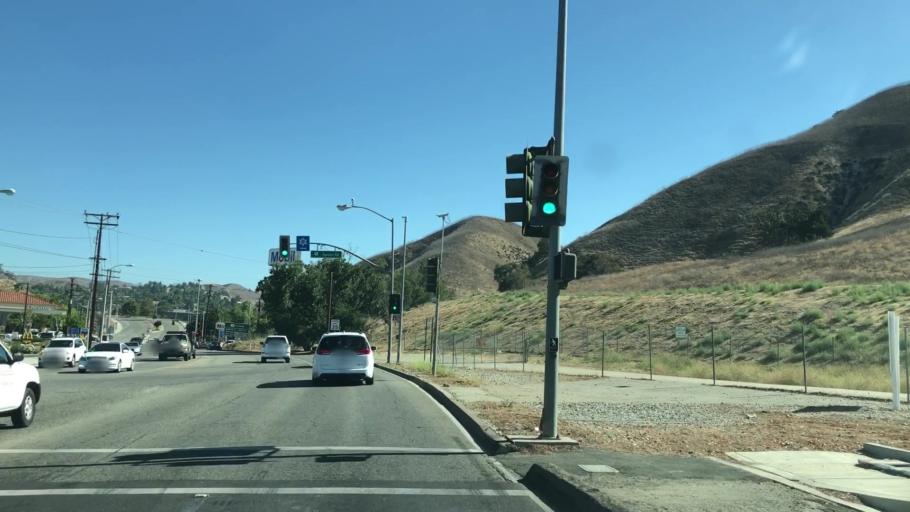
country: US
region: California
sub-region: Los Angeles County
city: Agoura
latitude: 34.1436
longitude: -118.6983
